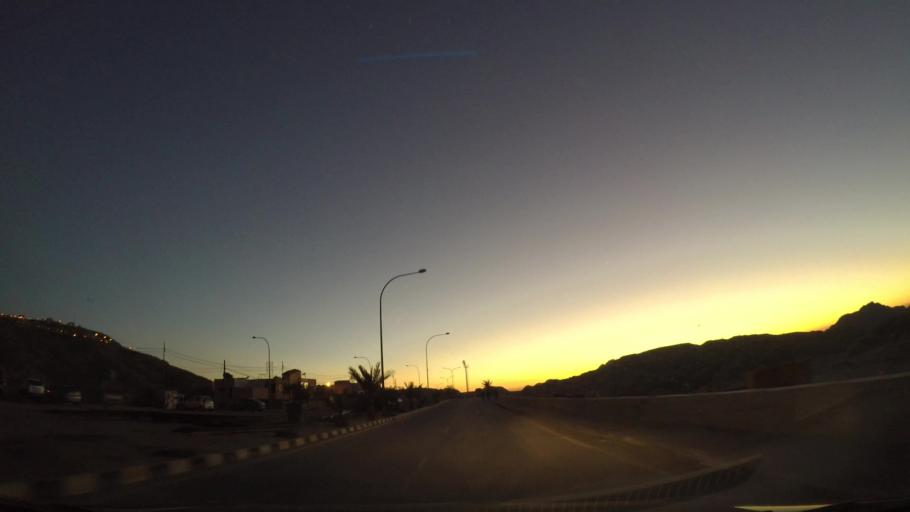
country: JO
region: Ma'an
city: Petra
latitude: 30.3286
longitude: 35.4698
